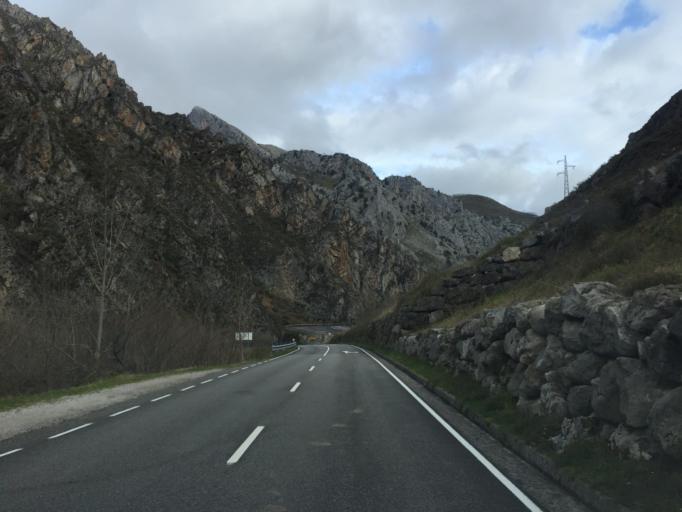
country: ES
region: Asturias
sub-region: Province of Asturias
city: Carrena
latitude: 43.2743
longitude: -4.8332
